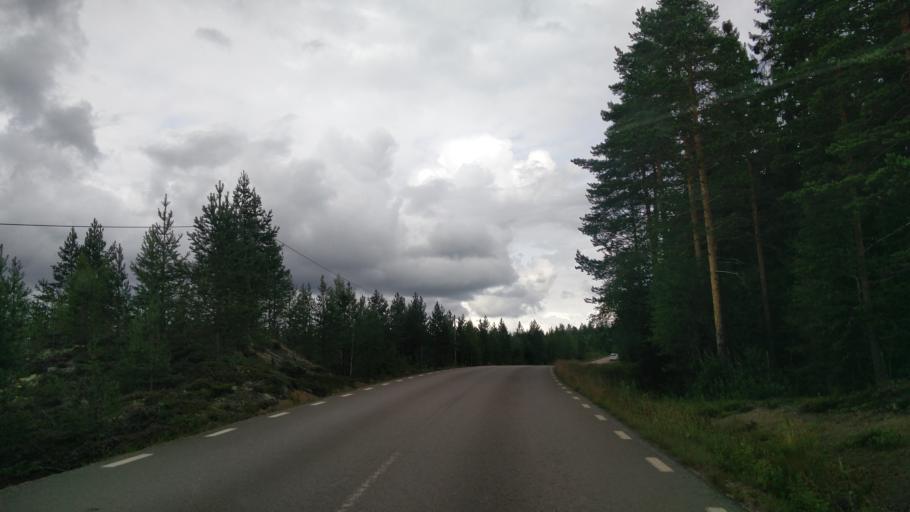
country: NO
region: Hedmark
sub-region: Trysil
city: Innbygda
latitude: 61.1578
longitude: 12.8166
